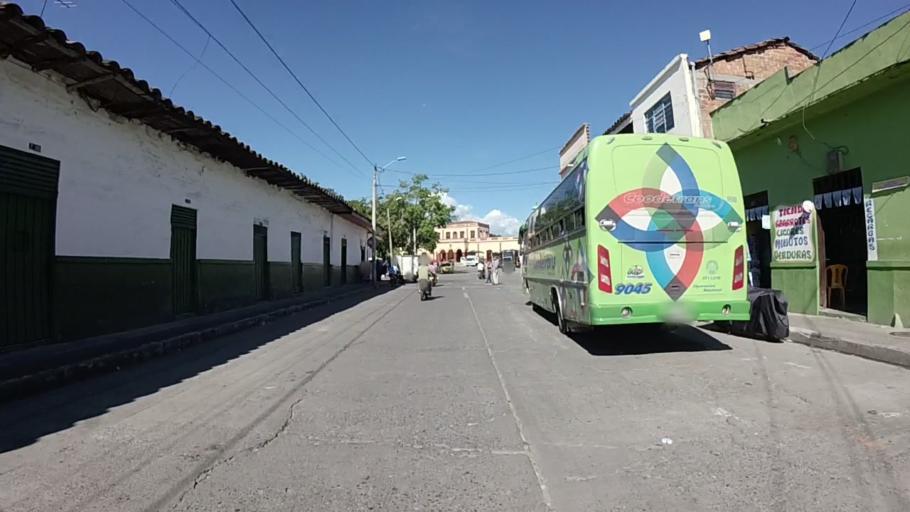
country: CO
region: Valle del Cauca
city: Cartago
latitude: 4.7455
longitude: -75.9083
